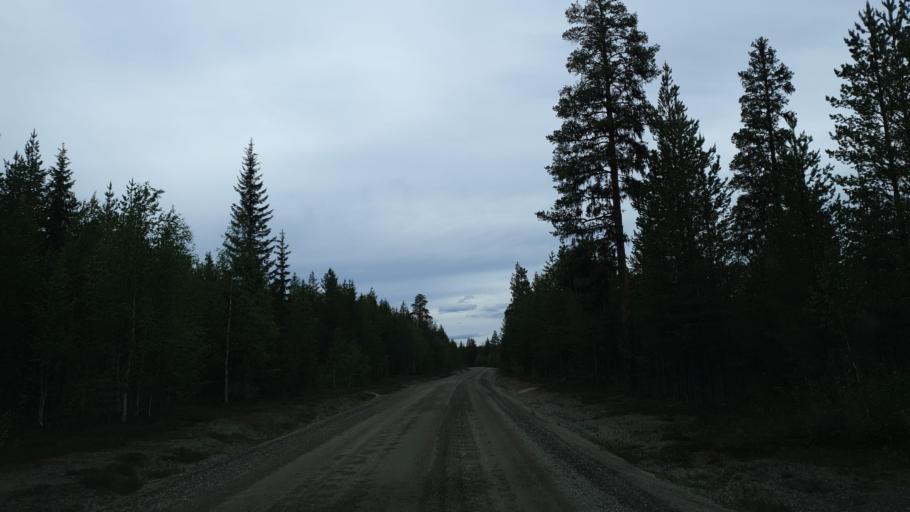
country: SE
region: Vaesterbotten
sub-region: Sorsele Kommun
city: Sorsele
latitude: 65.5529
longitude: 17.5073
